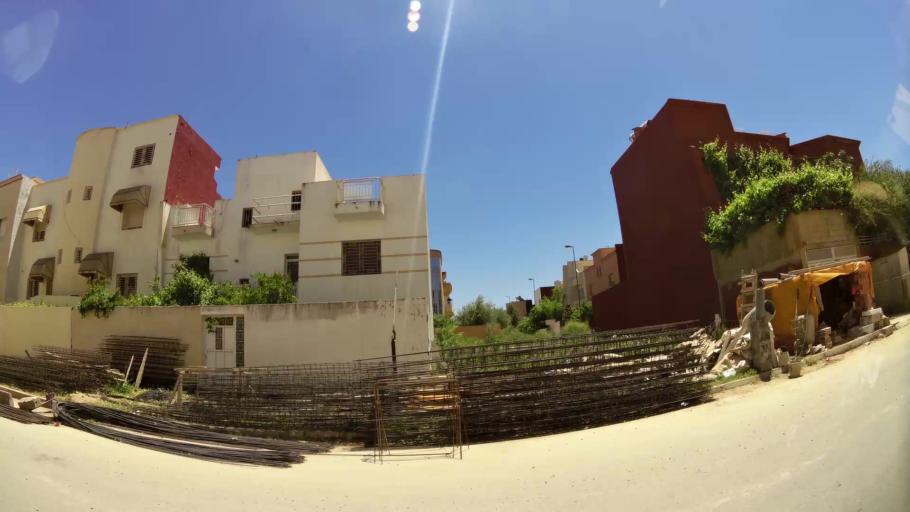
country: MA
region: Meknes-Tafilalet
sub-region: Meknes
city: Meknes
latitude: 33.8545
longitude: -5.5628
